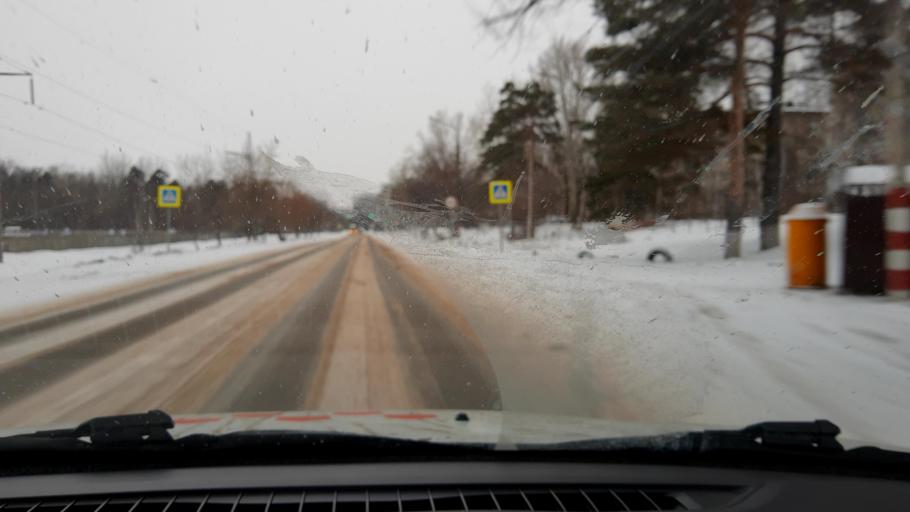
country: RU
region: Nizjnij Novgorod
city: Bor
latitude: 56.3307
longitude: 44.1178
